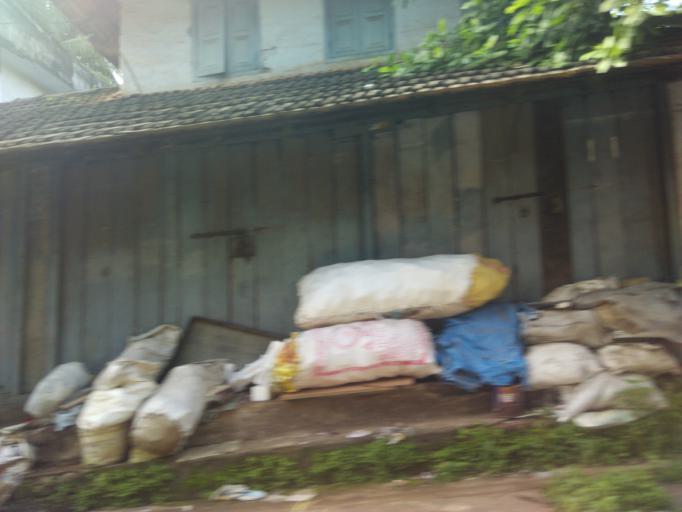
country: IN
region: Kerala
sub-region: Kozhikode
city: Kozhikode
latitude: 11.2911
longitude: 75.8135
